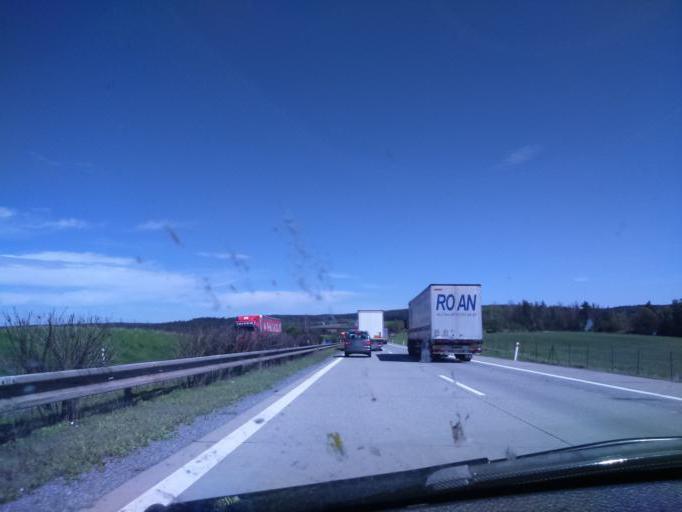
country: CZ
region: Plzensky
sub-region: Okres Tachov
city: Kladruby
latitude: 49.7051
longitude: 12.9632
